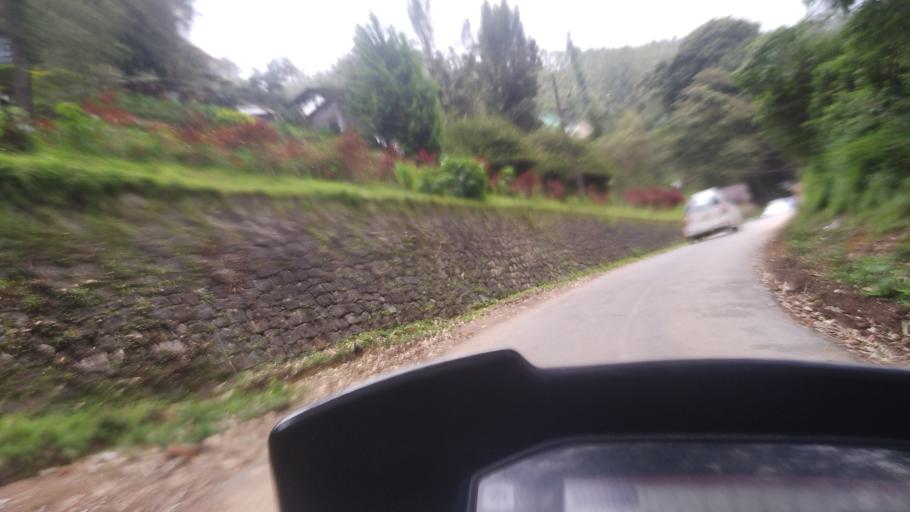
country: IN
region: Kerala
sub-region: Idukki
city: Munnar
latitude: 10.0671
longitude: 77.1049
